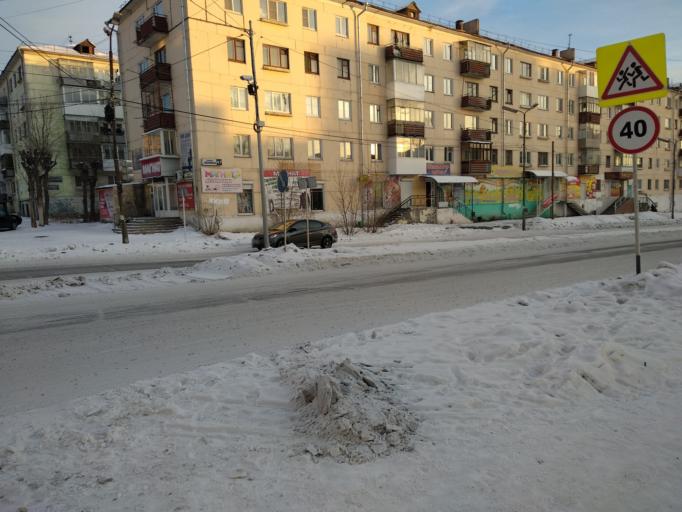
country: RU
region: Sverdlovsk
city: Krasnotur'insk
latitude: 59.7627
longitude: 60.2062
